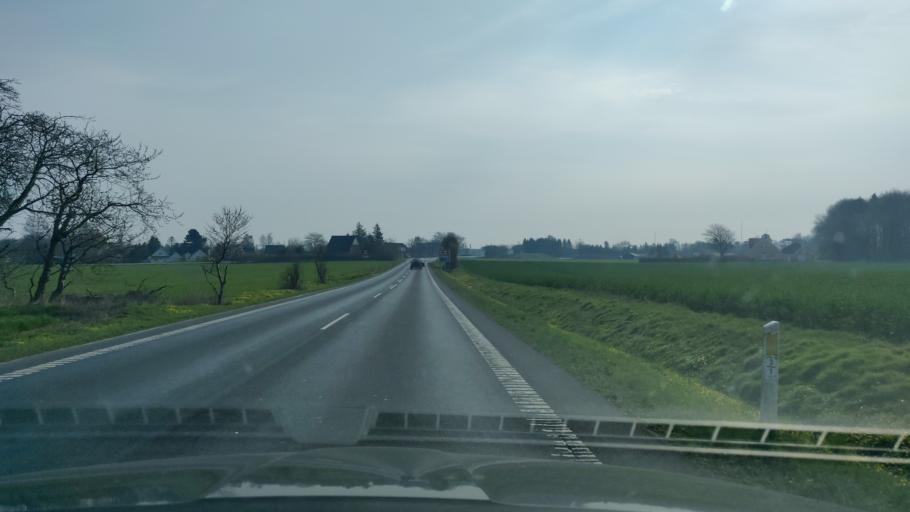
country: DK
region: South Denmark
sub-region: Fredericia Kommune
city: Snoghoj
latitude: 55.5353
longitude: 9.6863
